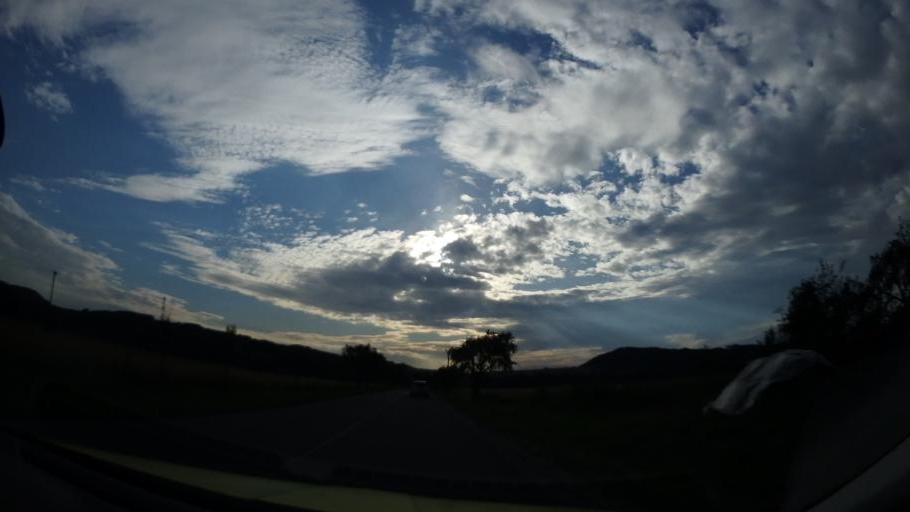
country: CZ
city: Stramberk
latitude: 49.5935
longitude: 18.1079
